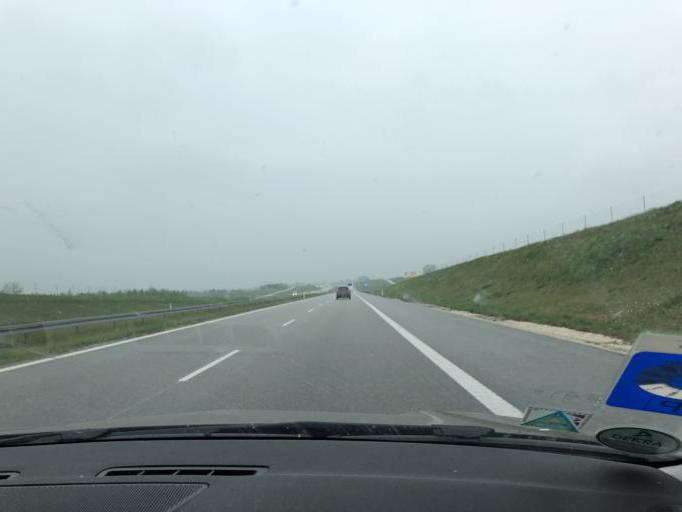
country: PL
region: Subcarpathian Voivodeship
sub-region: Powiat debicki
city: Czarna
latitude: 50.0928
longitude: 21.2978
